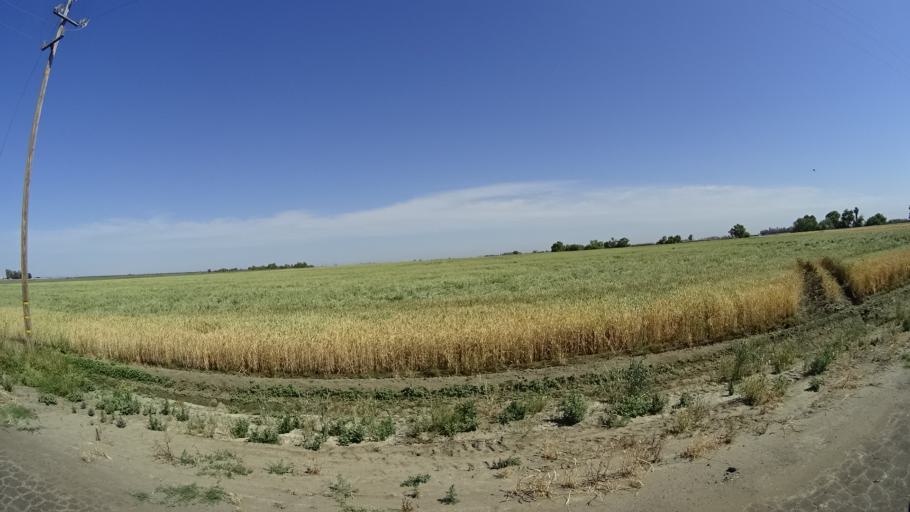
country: US
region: California
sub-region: Kings County
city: Stratford
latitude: 36.1968
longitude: -119.8237
